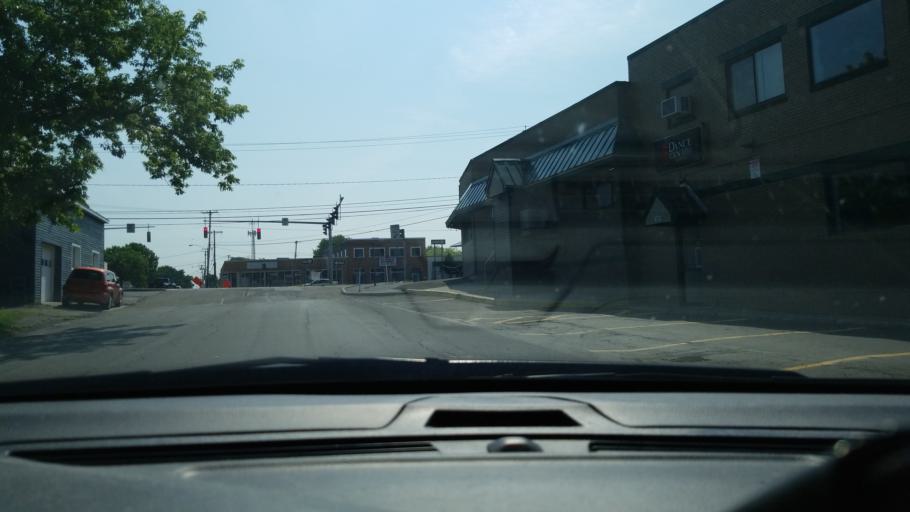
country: US
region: New York
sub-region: Onondaga County
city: Mattydale
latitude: 43.0977
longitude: -76.1463
